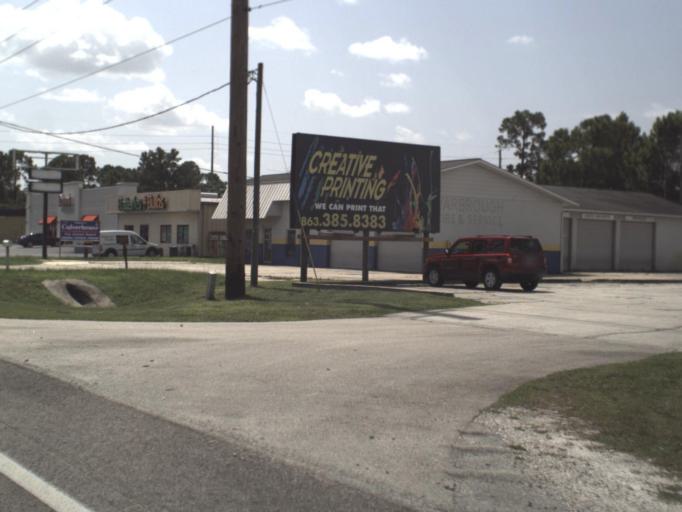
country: US
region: Florida
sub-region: Highlands County
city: Sebring
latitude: 27.5015
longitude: -81.4903
